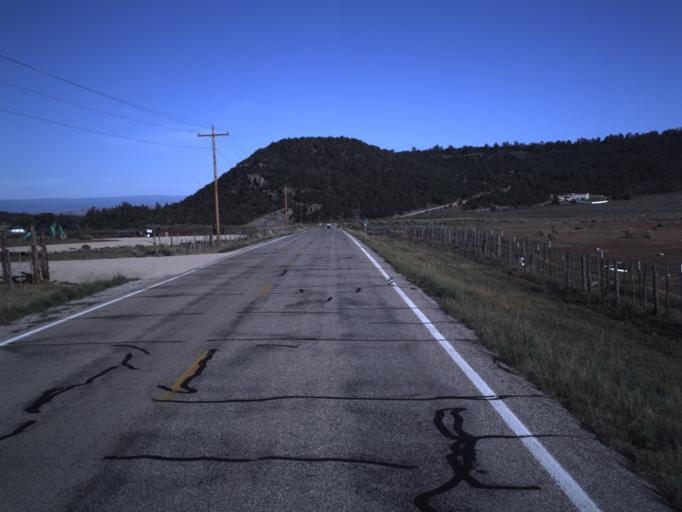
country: US
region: Utah
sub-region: Grand County
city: Moab
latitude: 38.3280
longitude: -109.1333
